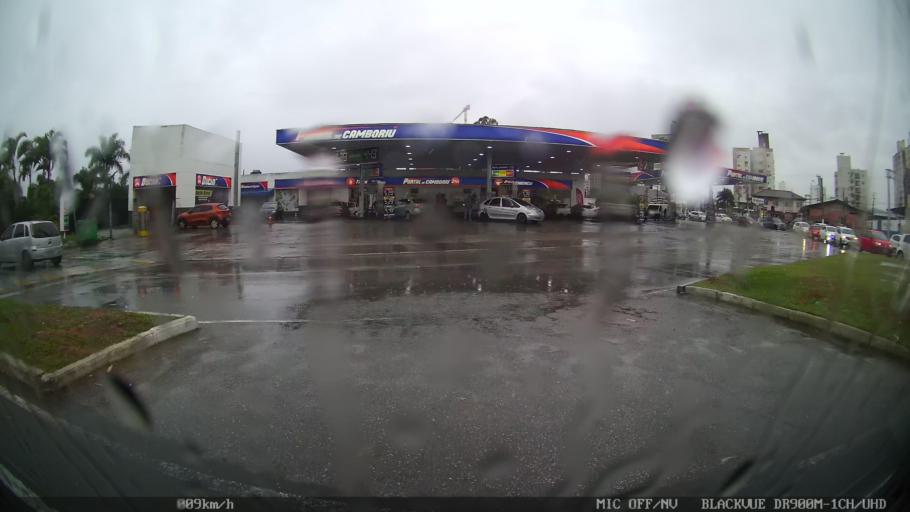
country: BR
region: Santa Catarina
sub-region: Balneario Camboriu
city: Balneario Camboriu
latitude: -27.0008
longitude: -48.6465
